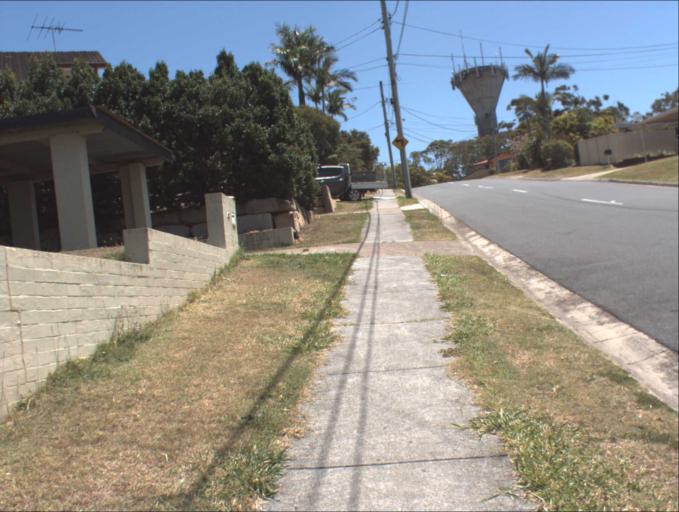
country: AU
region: Queensland
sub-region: Logan
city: Springwood
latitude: -27.6012
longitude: 153.1336
